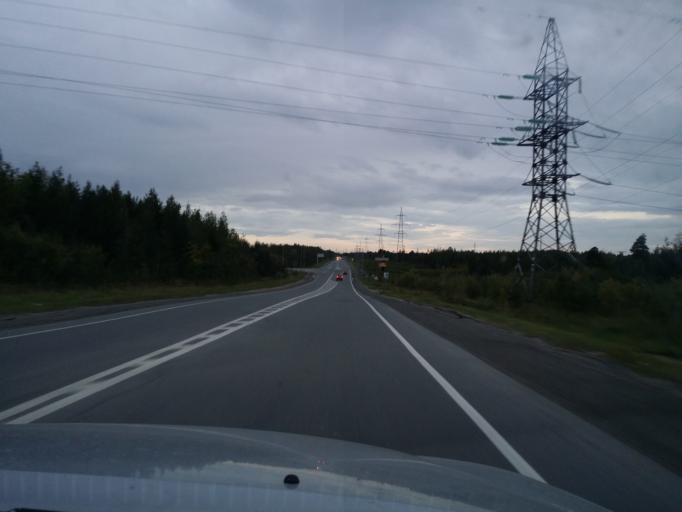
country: RU
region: Khanty-Mansiyskiy Avtonomnyy Okrug
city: Nizhnevartovsk
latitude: 60.9667
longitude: 76.6638
